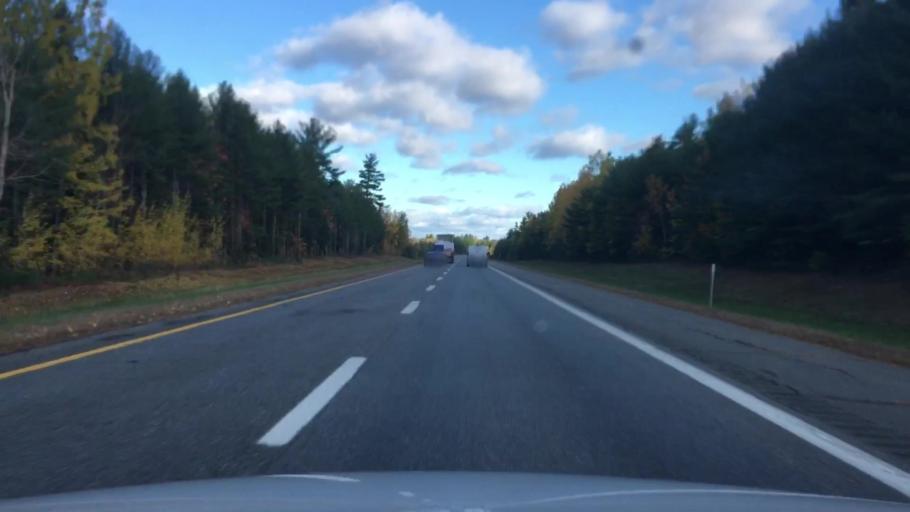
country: US
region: Maine
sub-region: Penobscot County
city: Greenbush
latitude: 45.1423
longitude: -68.7010
